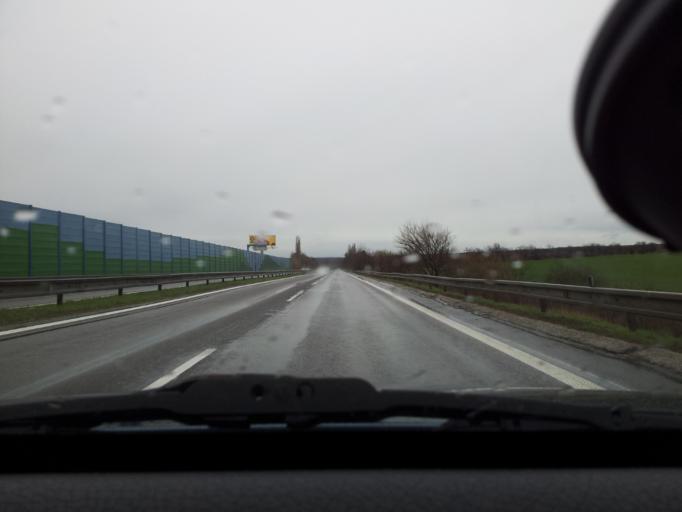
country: SK
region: Nitriansky
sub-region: Okres Nitra
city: Nitra
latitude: 48.3211
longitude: 17.9896
